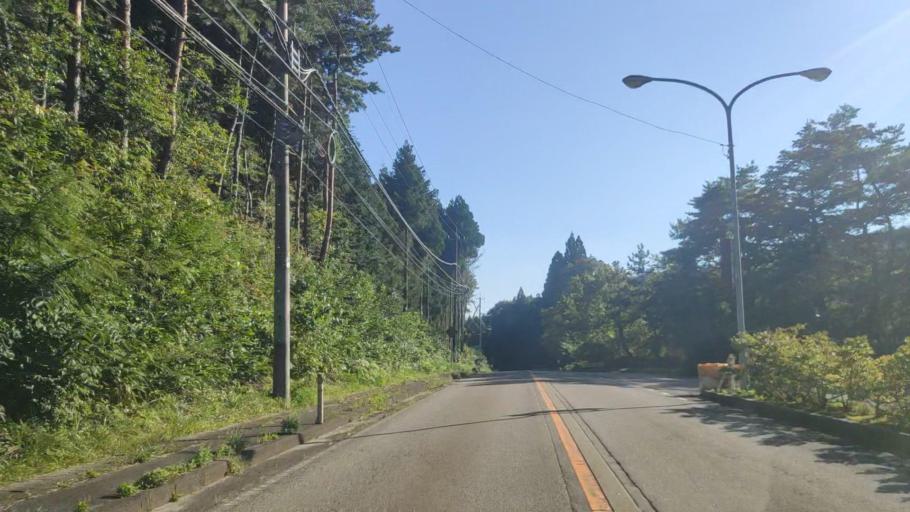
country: JP
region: Ishikawa
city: Nanao
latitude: 37.1293
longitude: 136.8638
